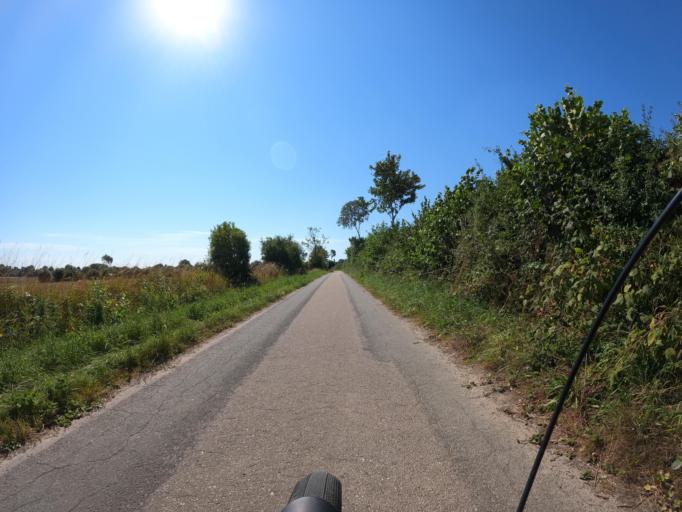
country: DE
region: Schleswig-Holstein
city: Steinberg
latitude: 54.7607
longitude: 9.7788
